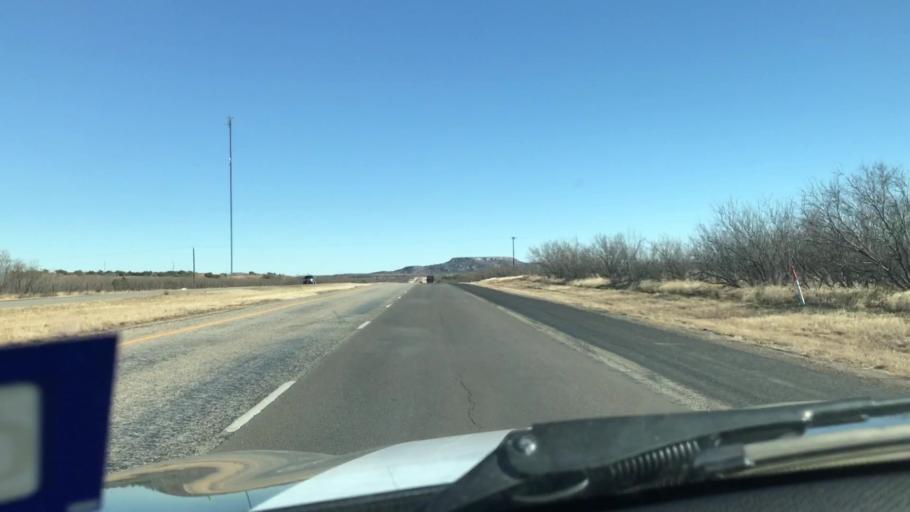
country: US
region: Texas
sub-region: Garza County
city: Post
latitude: 32.9864
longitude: -101.1319
